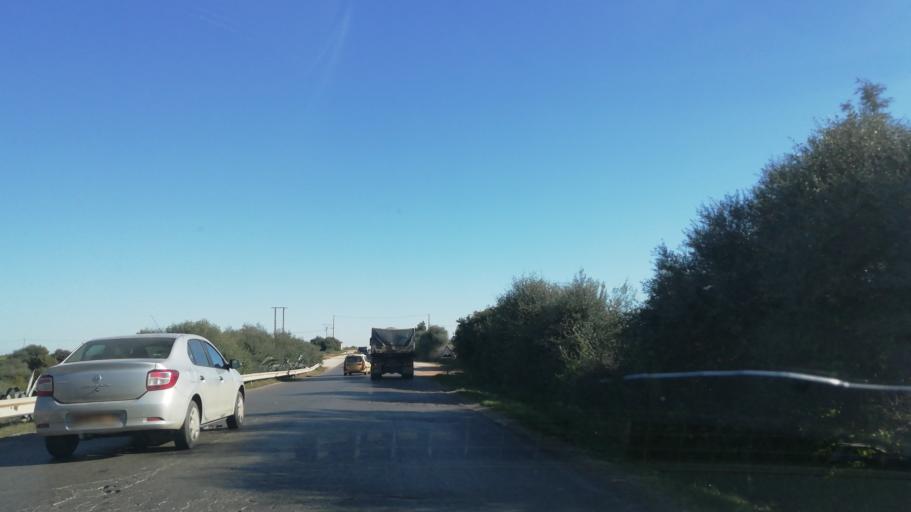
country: DZ
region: Relizane
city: Smala
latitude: 35.6935
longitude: 0.7839
